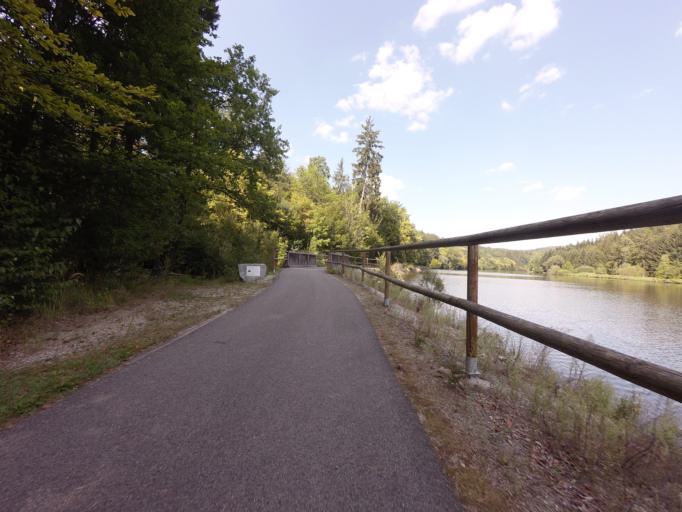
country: CZ
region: Jihocesky
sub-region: Okres Ceske Budejovice
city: Hluboka nad Vltavou
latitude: 49.0776
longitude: 14.4542
